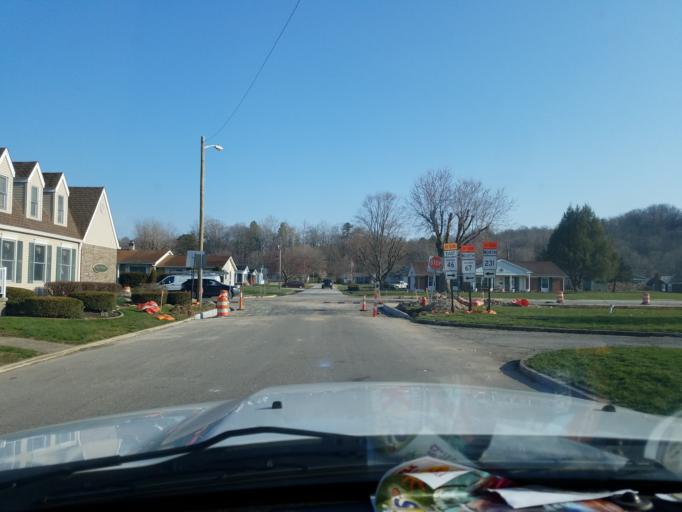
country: US
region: Indiana
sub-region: Owen County
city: Spencer
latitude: 39.2867
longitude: -86.7543
